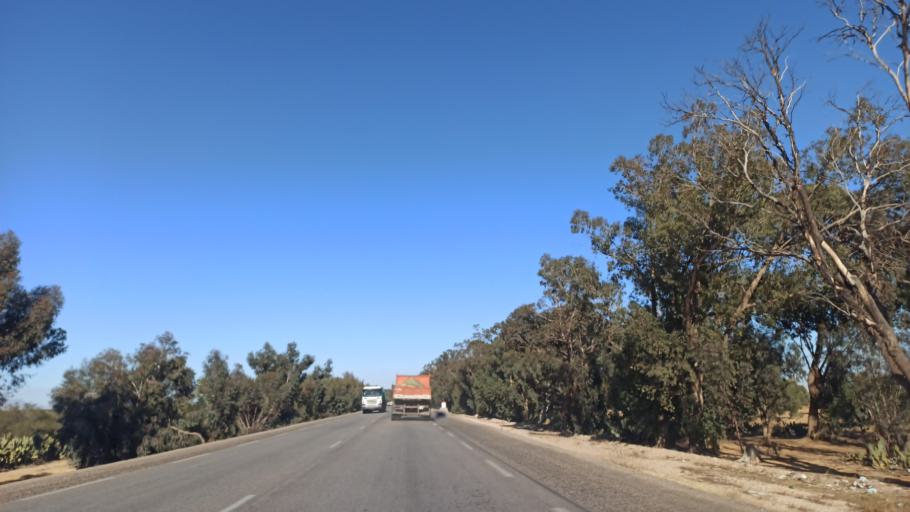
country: TN
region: Sidi Bu Zayd
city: Jilma
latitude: 35.1744
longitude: 9.3716
